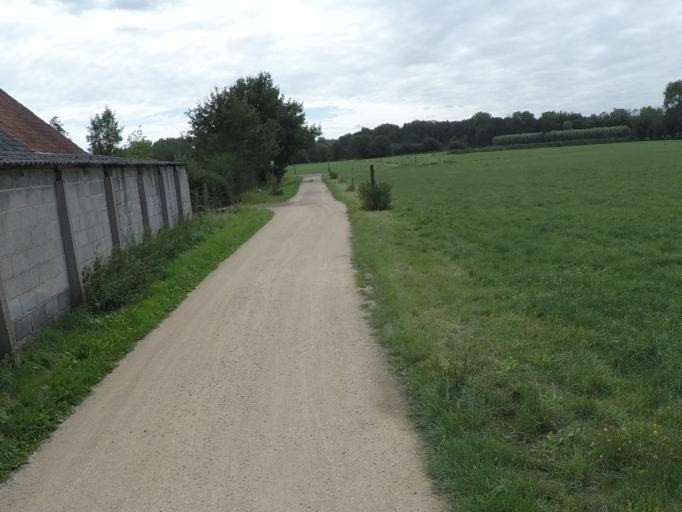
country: BE
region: Flanders
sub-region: Provincie Antwerpen
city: Zandhoven
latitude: 51.2183
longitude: 4.6749
